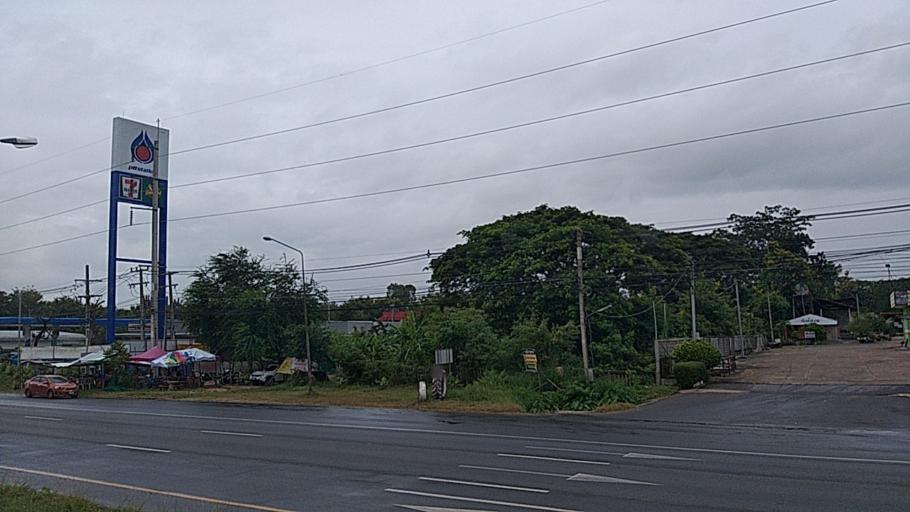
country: TH
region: Maha Sarakham
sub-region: Amphoe Borabue
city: Borabue
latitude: 16.0521
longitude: 103.1301
